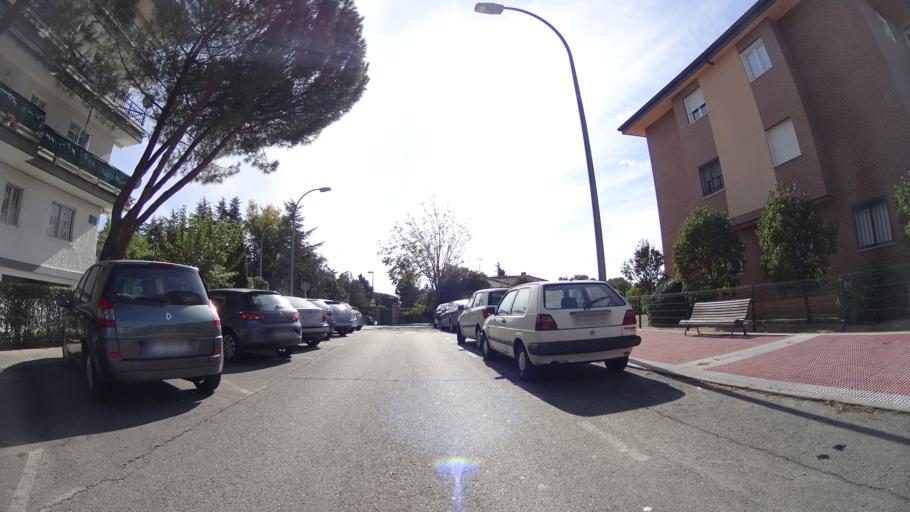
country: ES
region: Madrid
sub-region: Provincia de Madrid
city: Collado-Villalba
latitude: 40.6177
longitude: -4.0138
